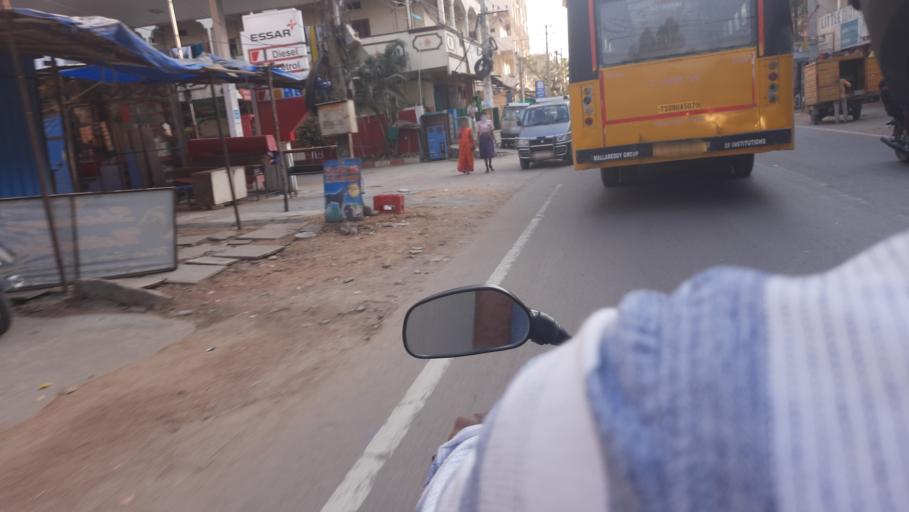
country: IN
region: Telangana
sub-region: Rangareddi
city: Secunderabad
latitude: 17.5040
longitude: 78.5399
